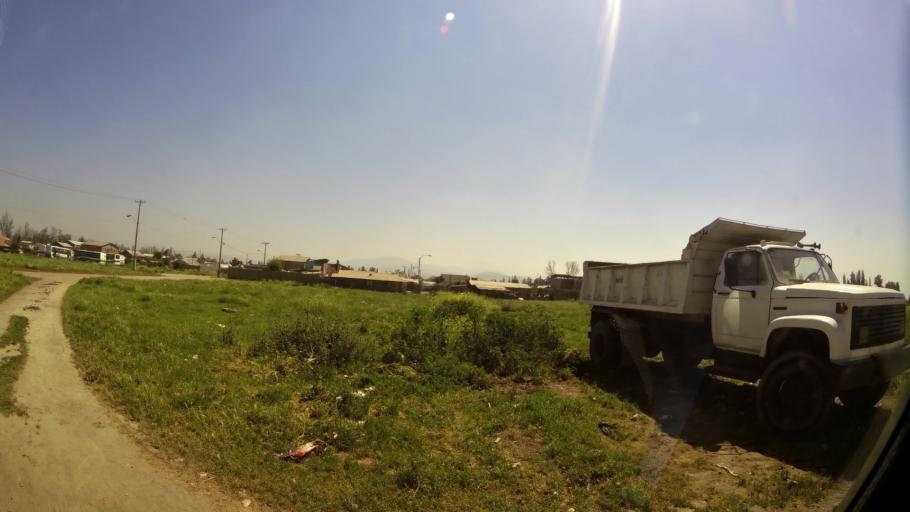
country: CL
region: Santiago Metropolitan
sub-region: Provincia de Talagante
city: Penaflor
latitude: -33.5930
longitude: -70.8091
